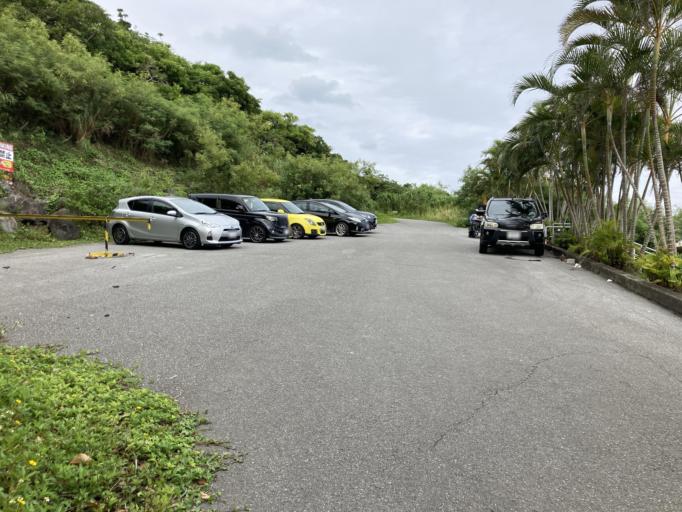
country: JP
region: Okinawa
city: Tomigusuku
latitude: 26.1404
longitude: 127.7968
